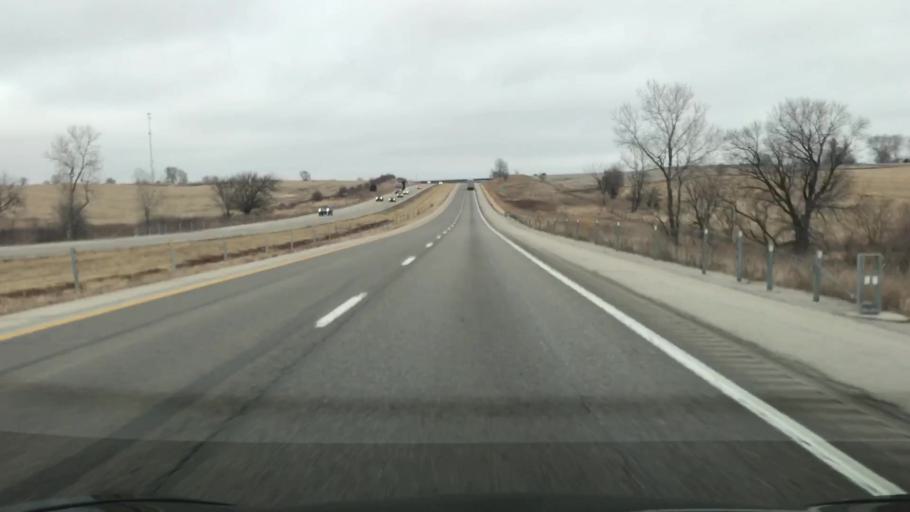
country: US
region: Iowa
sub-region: Madison County
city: Earlham
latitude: 41.5019
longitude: -94.2108
